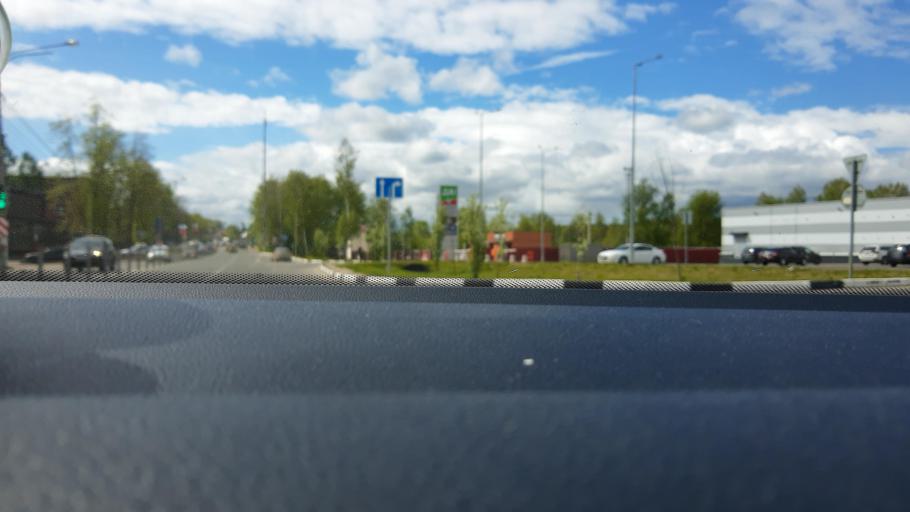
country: RU
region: Moskovskaya
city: Dmitrov
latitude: 56.3359
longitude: 37.5120
